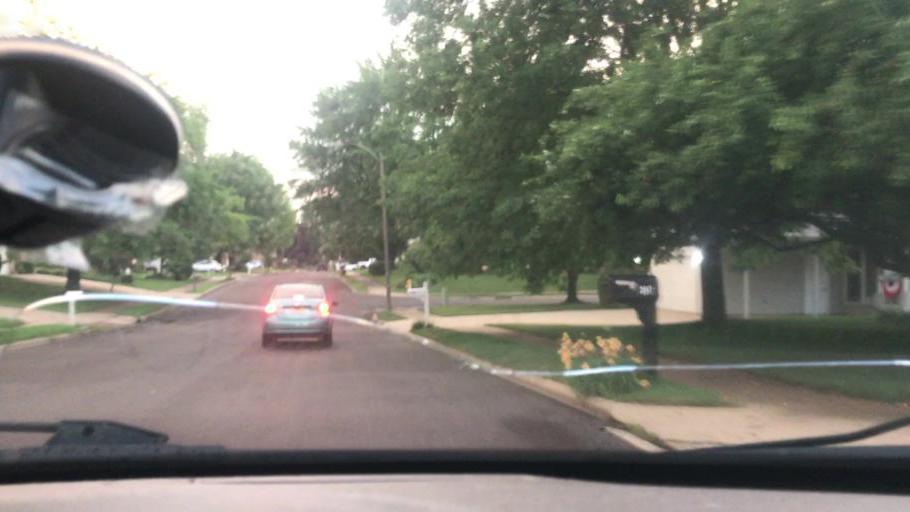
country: US
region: Illinois
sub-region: Tazewell County
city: Pekin
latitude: 40.5423
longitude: -89.6191
